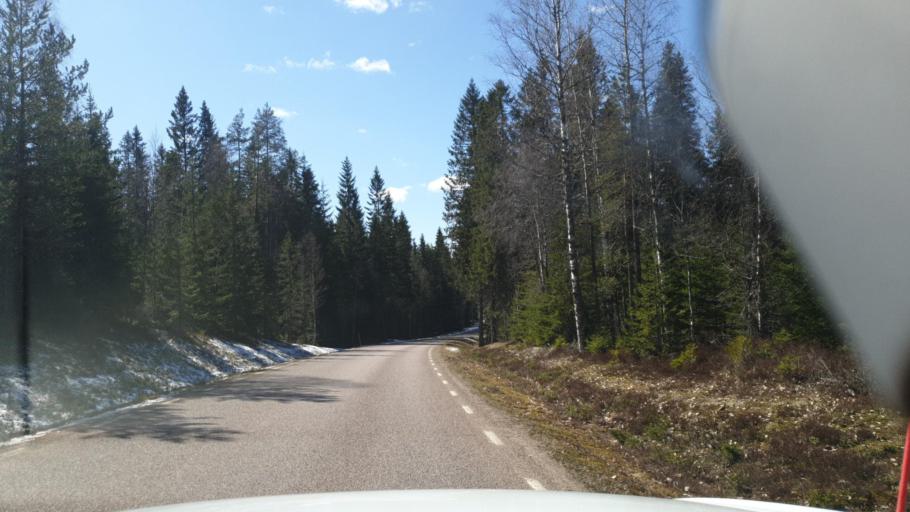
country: SE
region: Vaermland
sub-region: Arvika Kommun
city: Arvika
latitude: 59.8194
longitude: 12.8391
